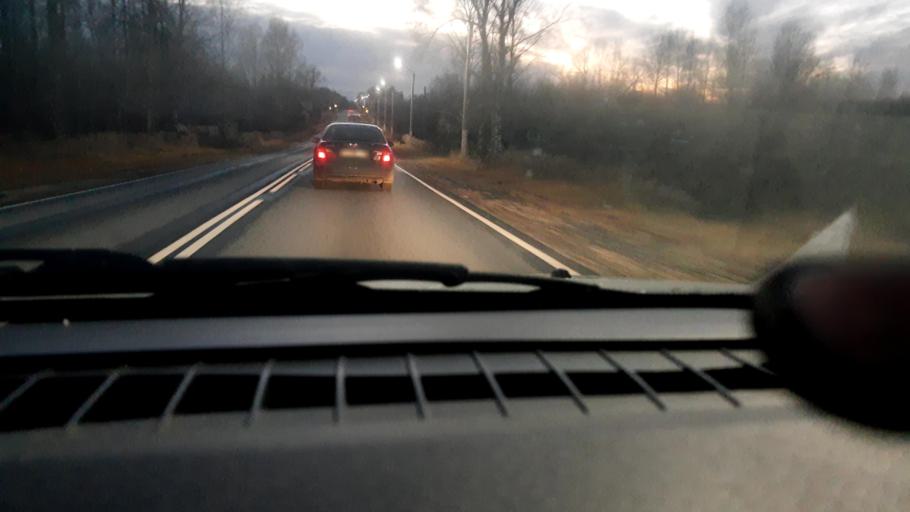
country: RU
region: Nizjnij Novgorod
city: Sukhobezvodnoye
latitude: 56.8708
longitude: 44.9400
